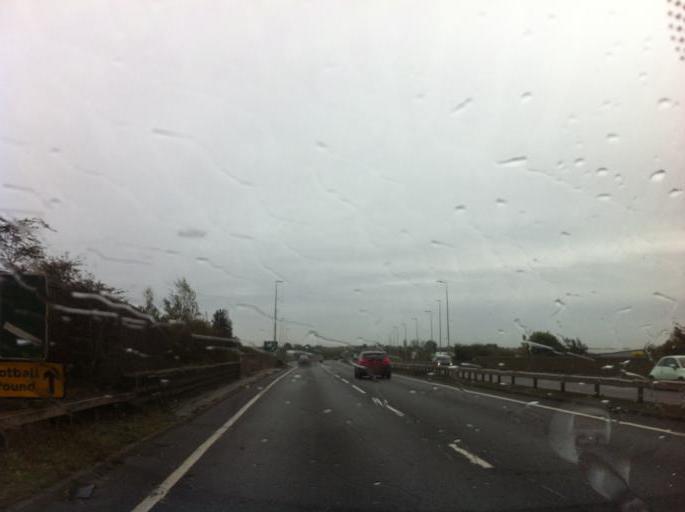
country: GB
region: England
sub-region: Peterborough
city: Peterborough
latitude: 52.5485
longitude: -0.2463
